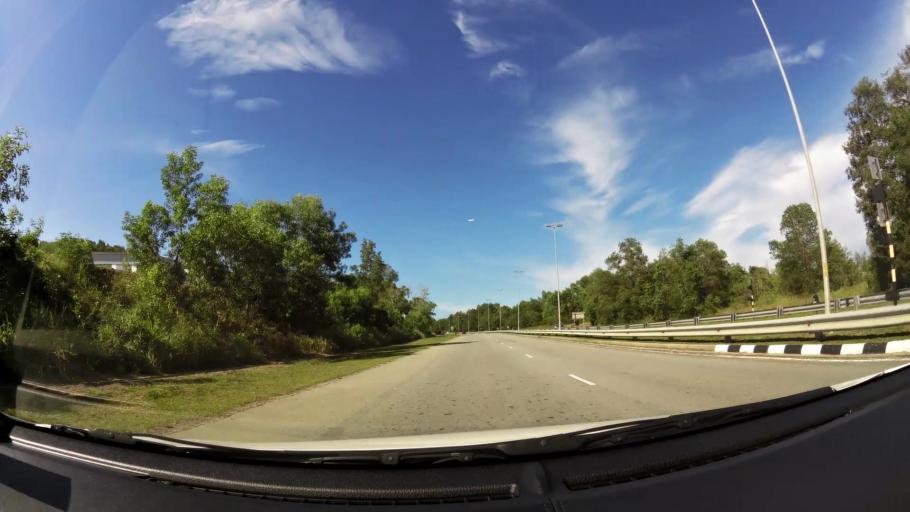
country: BN
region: Brunei and Muara
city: Bandar Seri Begawan
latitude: 4.9745
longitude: 114.9304
